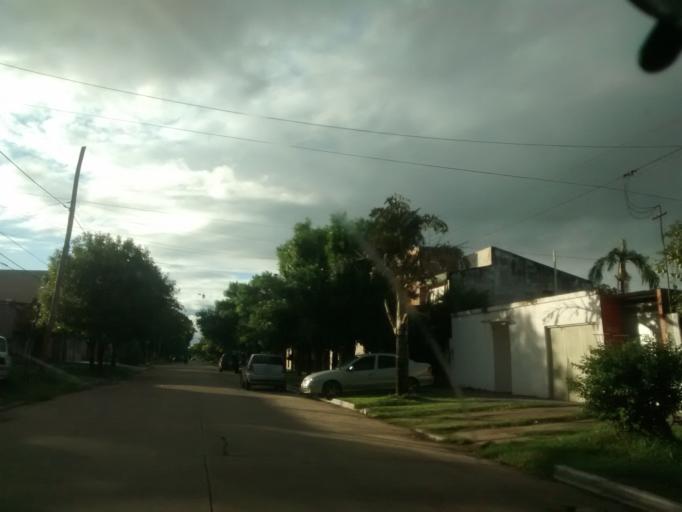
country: AR
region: Chaco
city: Resistencia
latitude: -27.4631
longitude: -58.9748
